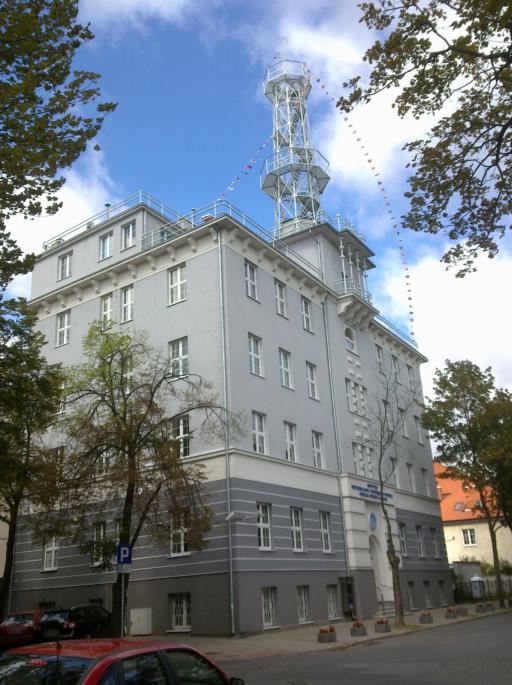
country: PL
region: Pomeranian Voivodeship
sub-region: Gdynia
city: Gdynia
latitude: 54.5204
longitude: 18.5467
